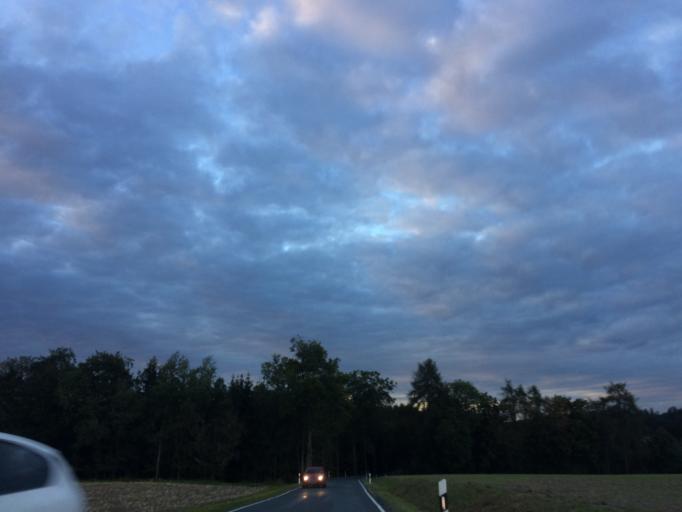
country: DE
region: Thuringia
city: Paska
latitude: 50.6295
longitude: 11.6439
